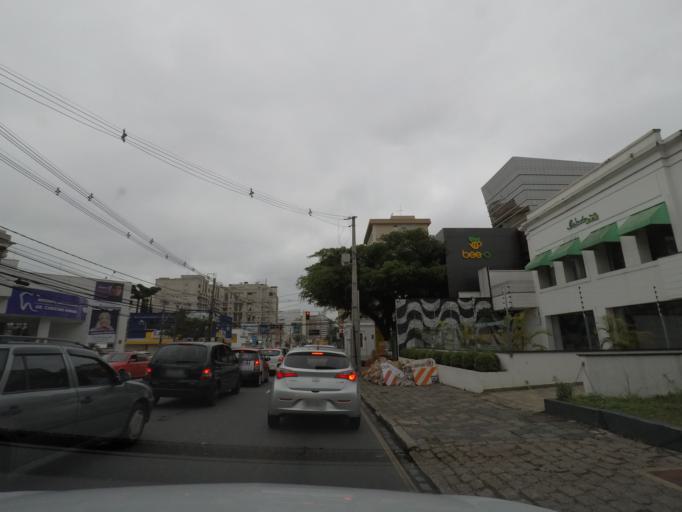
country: BR
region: Parana
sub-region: Curitiba
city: Curitiba
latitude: -25.4432
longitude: -49.2894
